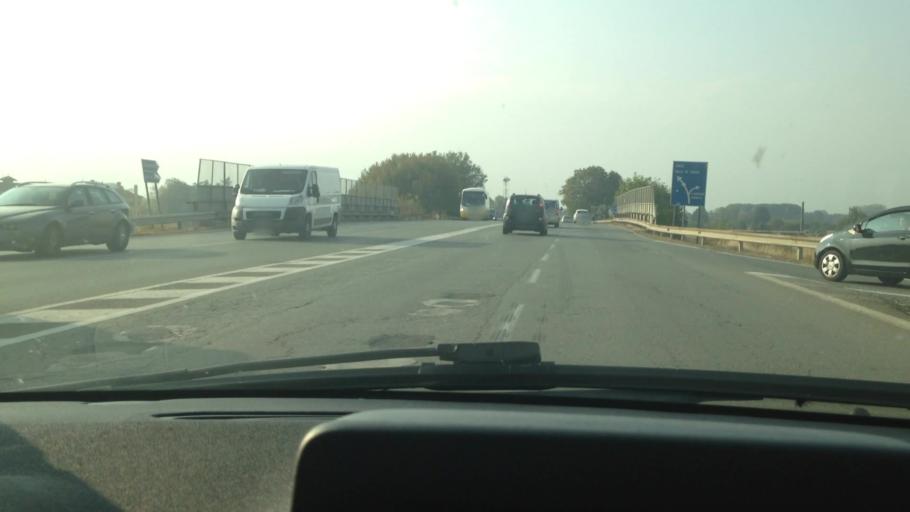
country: IT
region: Piedmont
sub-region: Provincia di Torino
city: Caselle Torinese
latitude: 45.1872
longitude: 7.6432
